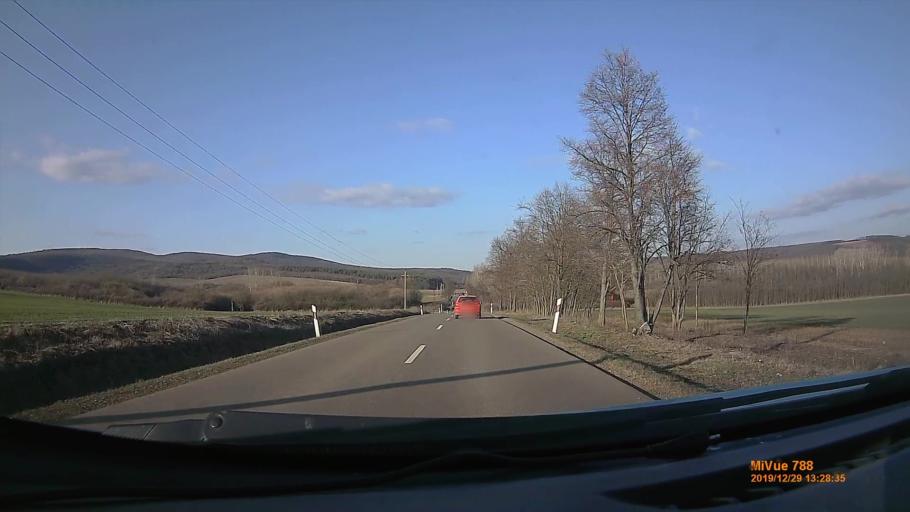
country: HU
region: Heves
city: Verpelet
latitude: 47.8641
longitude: 20.2024
